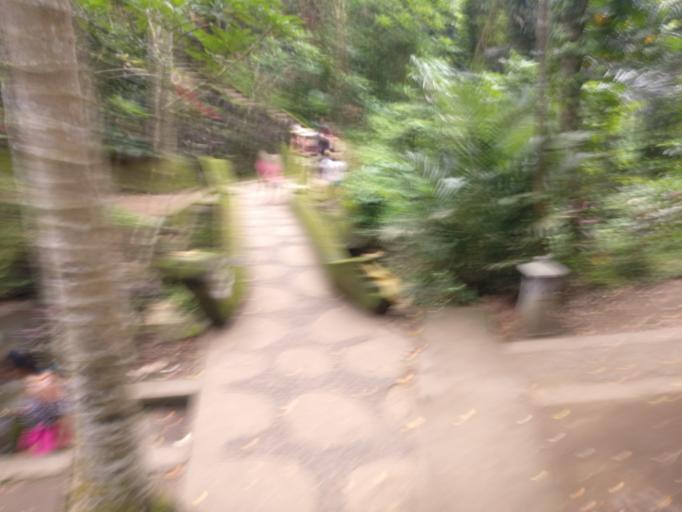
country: ID
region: Bali
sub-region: Kabupaten Gianyar
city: Ubud
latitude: -8.5238
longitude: 115.2865
